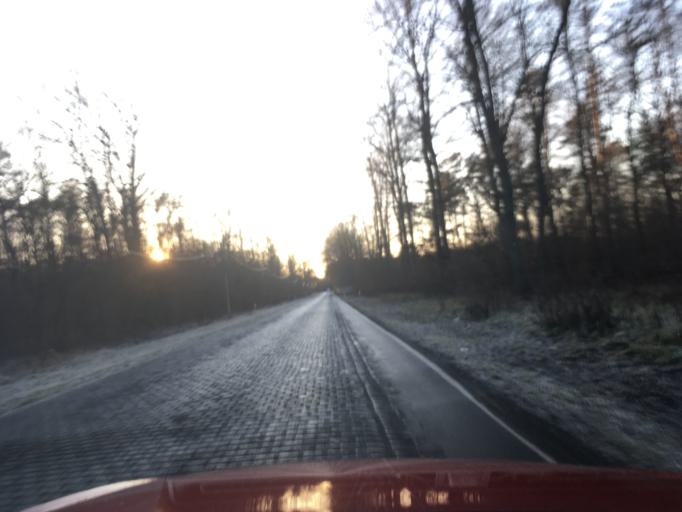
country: DE
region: Saxony-Anhalt
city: Rosslau
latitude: 51.9083
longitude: 12.2910
